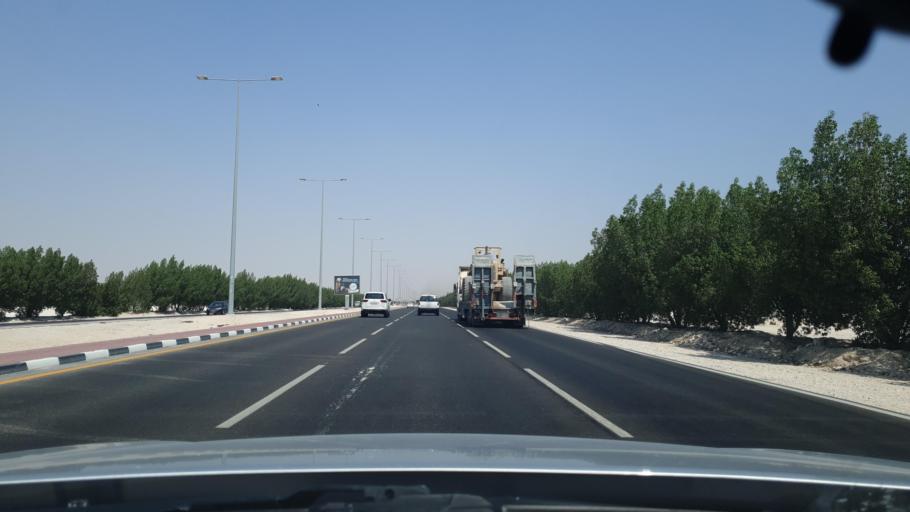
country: QA
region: Al Khawr
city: Al Khawr
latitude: 25.7005
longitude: 51.5032
